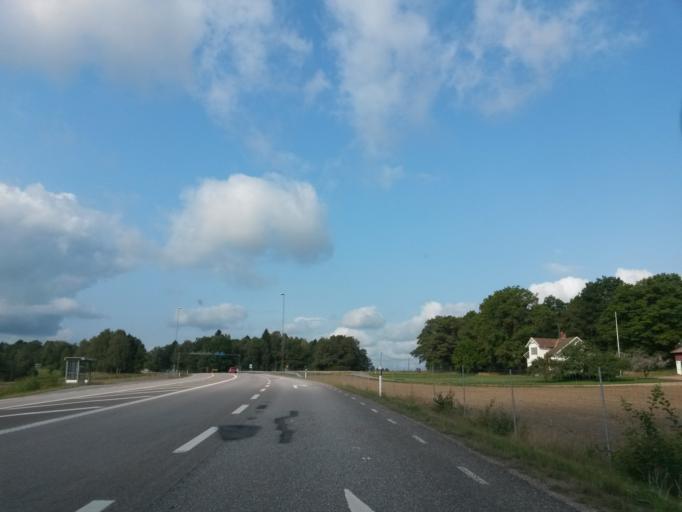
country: SE
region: Vaestra Goetaland
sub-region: Vargarda Kommun
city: Jonstorp
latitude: 58.0042
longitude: 12.7322
